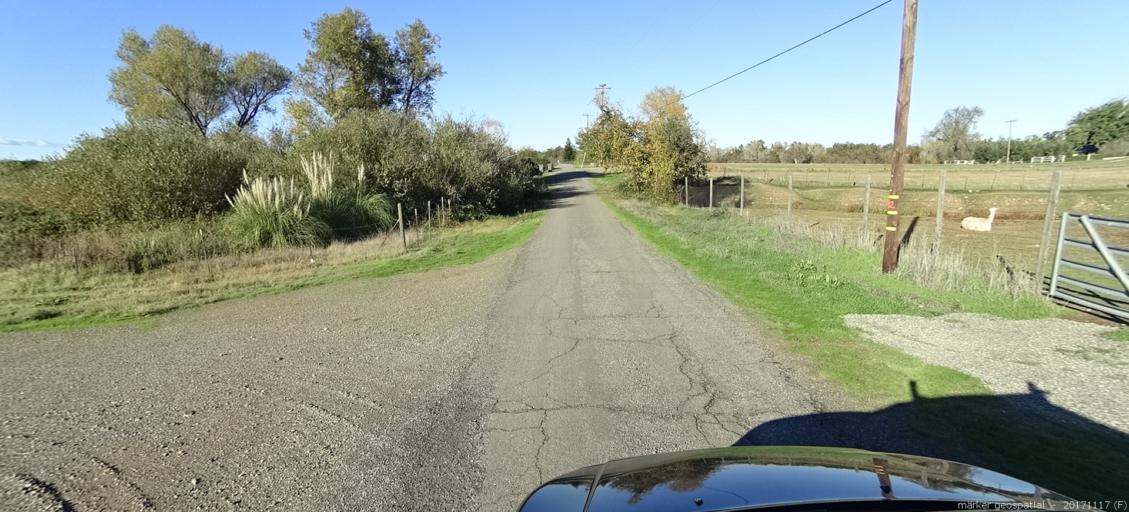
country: US
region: California
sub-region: Shasta County
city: Cottonwood
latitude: 40.3991
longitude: -122.2025
